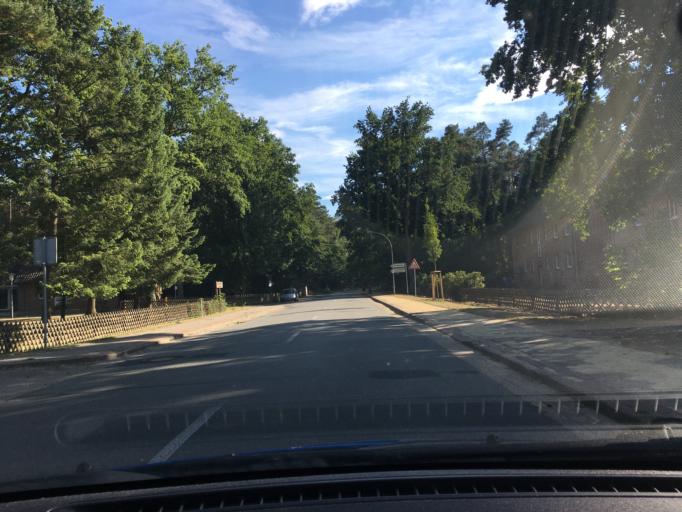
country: DE
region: Lower Saxony
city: Bleckede
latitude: 53.2810
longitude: 10.7237
